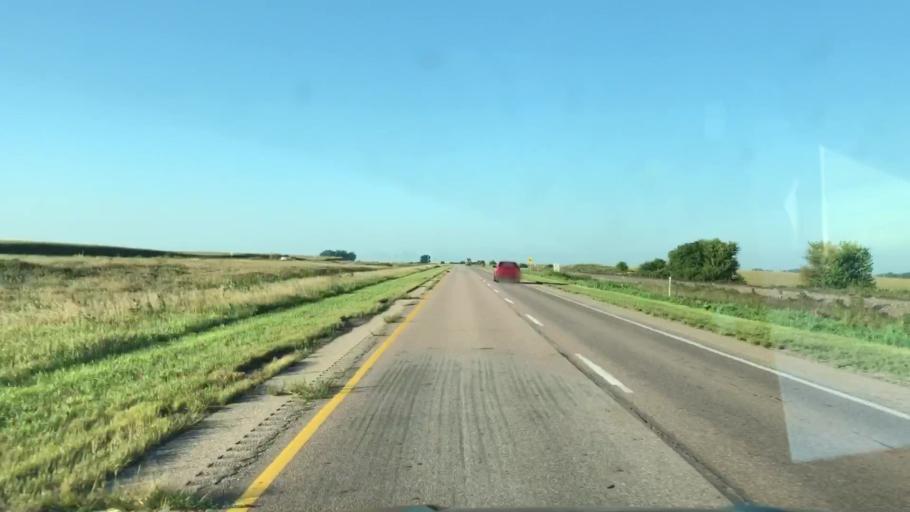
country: US
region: Iowa
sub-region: O'Brien County
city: Sheldon
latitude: 43.1158
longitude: -95.8939
